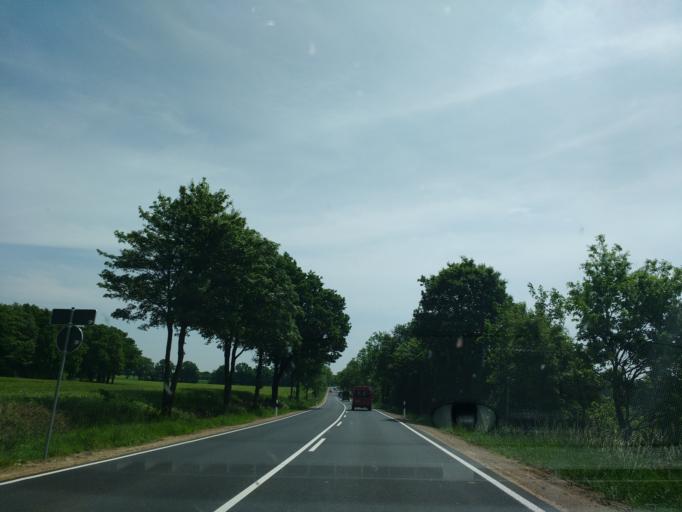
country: DE
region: Schleswig-Holstein
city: Braak
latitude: 53.5998
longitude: 10.2445
